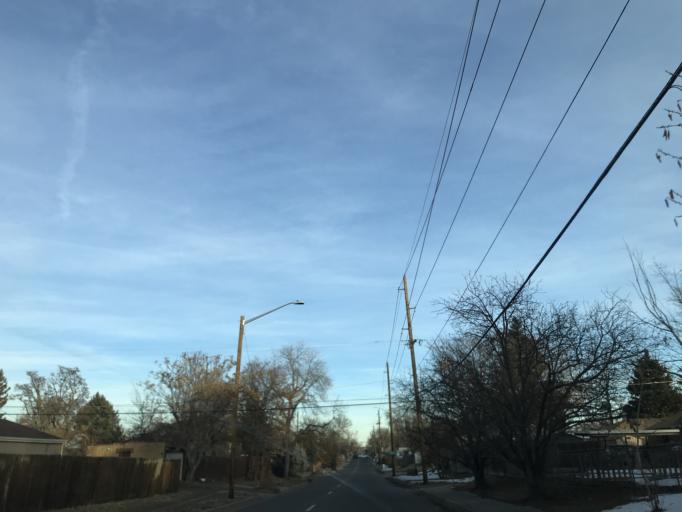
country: US
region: Colorado
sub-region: Arapahoe County
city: Glendale
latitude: 39.7387
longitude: -104.9023
